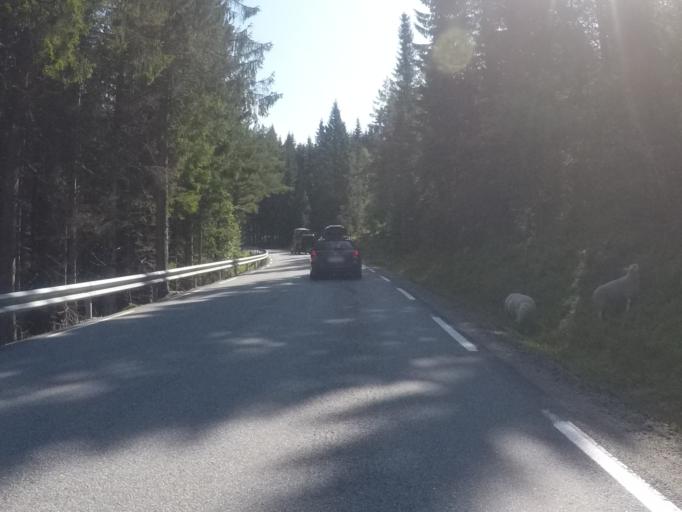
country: NO
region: Sogn og Fjordane
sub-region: Hornindal
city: Hornindal
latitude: 61.7949
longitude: 6.5295
